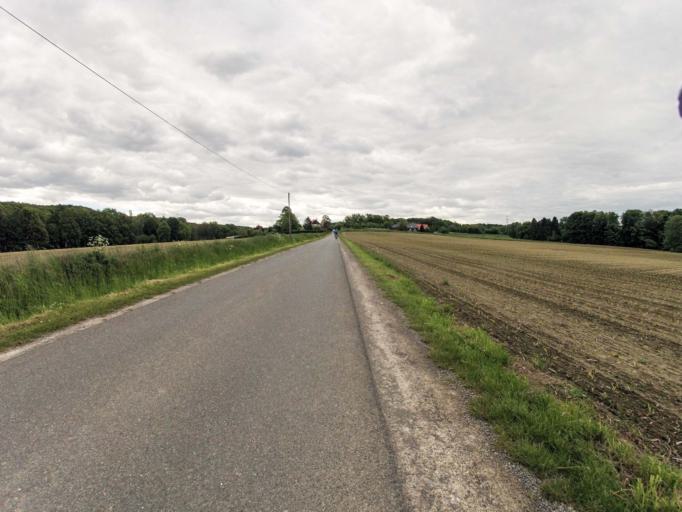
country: DE
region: Lower Saxony
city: Laar
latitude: 52.3284
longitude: 8.2754
